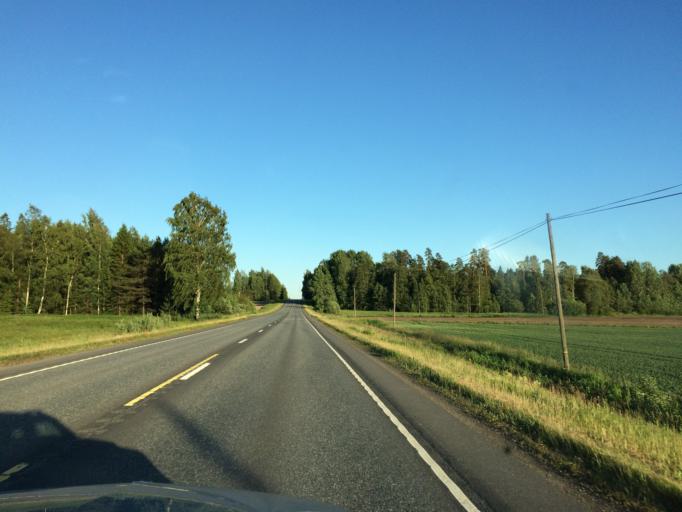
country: FI
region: Haeme
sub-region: Haemeenlinna
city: Tervakoski
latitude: 60.7946
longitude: 24.6697
